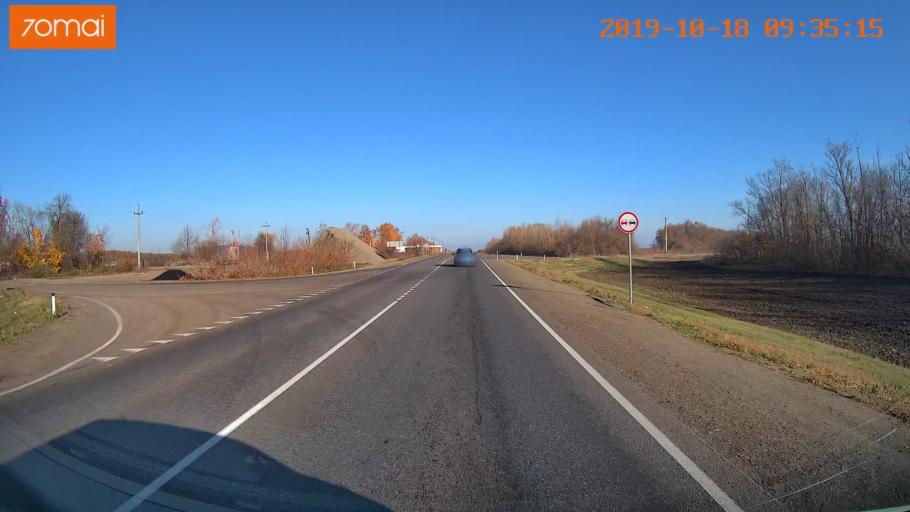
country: RU
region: Tula
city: Yefremov
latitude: 53.1901
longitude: 38.1492
